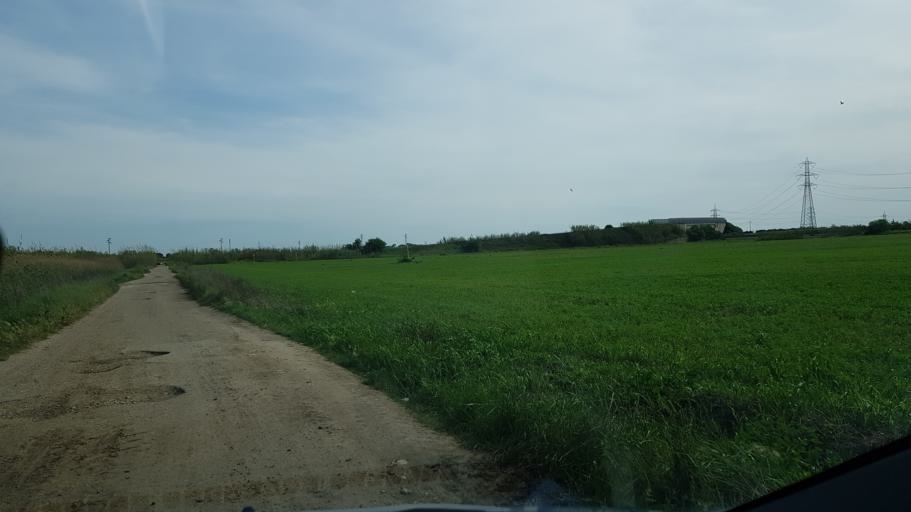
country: IT
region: Apulia
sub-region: Provincia di Brindisi
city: La Rosa
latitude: 40.6022
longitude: 17.9698
